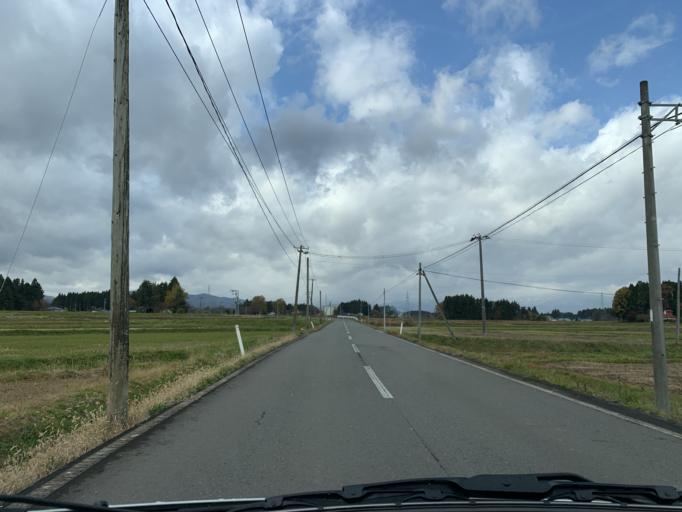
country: JP
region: Iwate
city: Mizusawa
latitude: 39.0643
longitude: 141.0908
